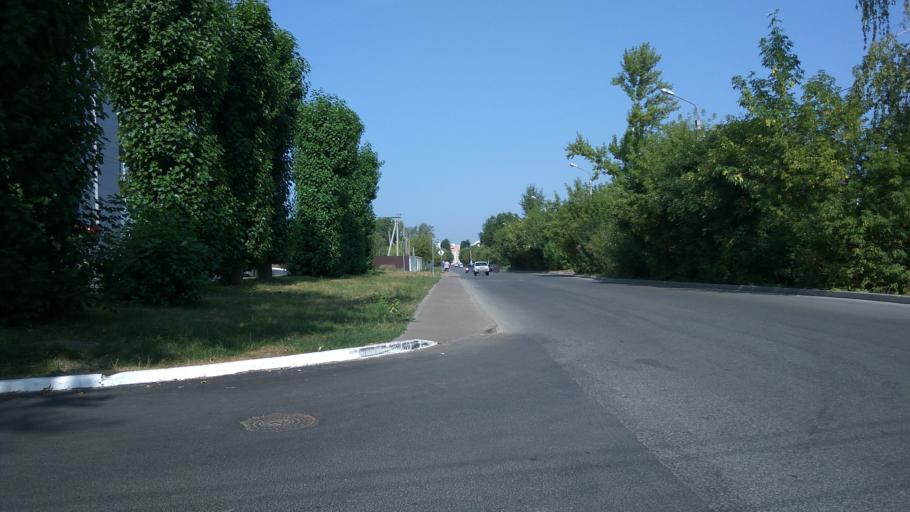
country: RU
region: Tatarstan
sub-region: Gorod Kazan'
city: Kazan
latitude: 55.7692
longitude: 49.1519
